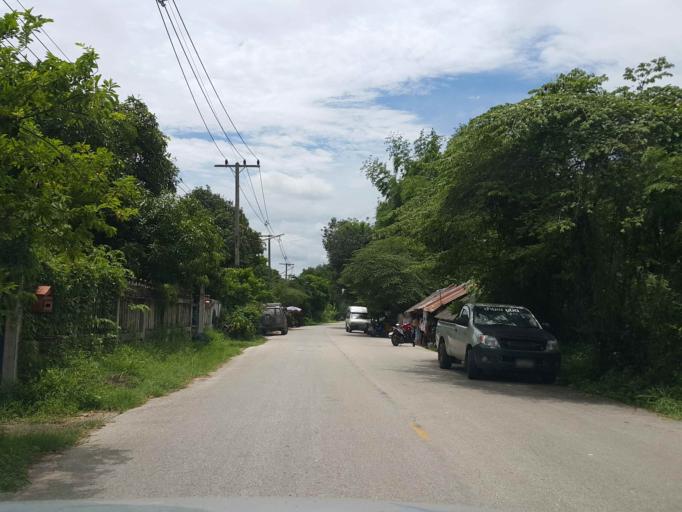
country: TH
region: Sukhothai
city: Ban Na
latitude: 17.0091
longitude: 99.7062
